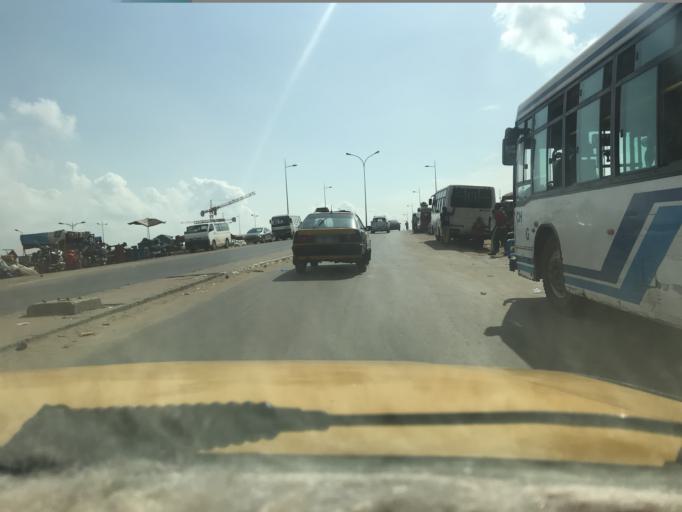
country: SN
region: Dakar
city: Dakar
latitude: 14.6979
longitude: -17.4435
